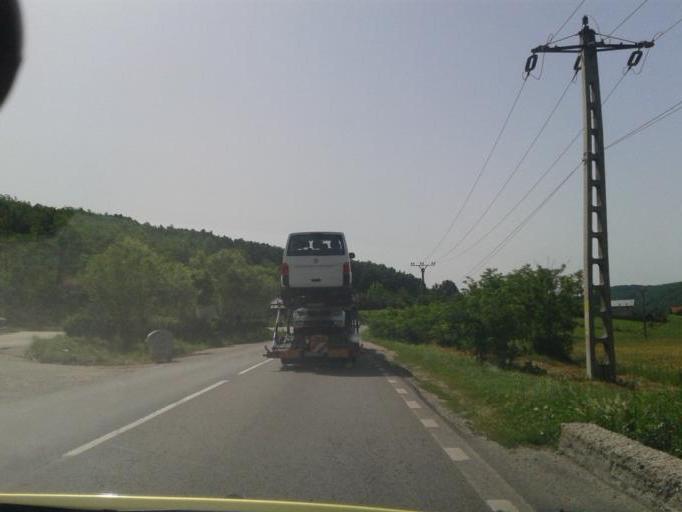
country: RO
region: Arges
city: Draganu-Olteni
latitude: 44.9506
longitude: 24.6979
